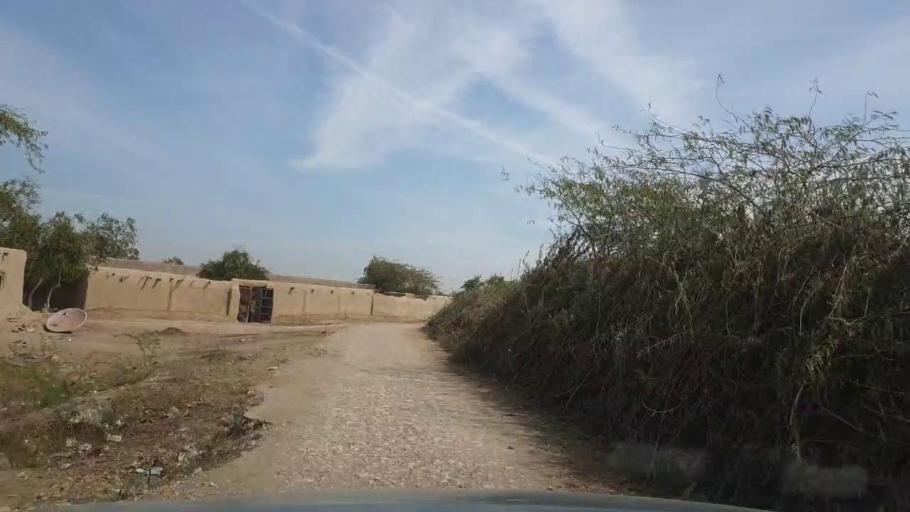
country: PK
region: Sindh
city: Nabisar
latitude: 25.1171
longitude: 69.6337
